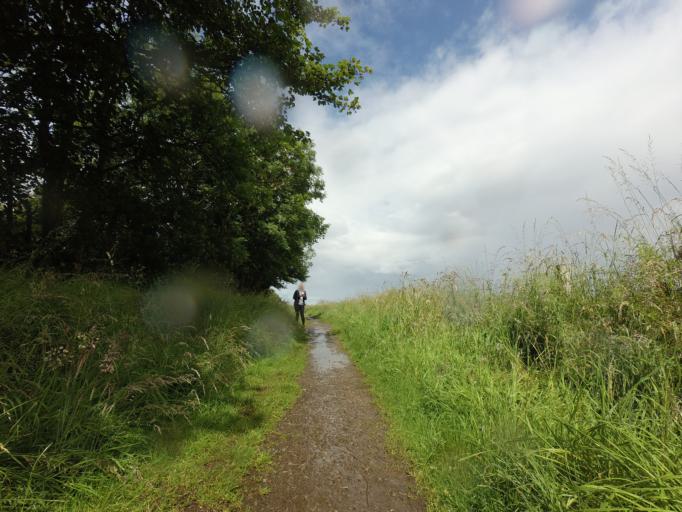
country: GB
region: Scotland
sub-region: Moray
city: Fochabers
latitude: 57.6690
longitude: -3.0908
